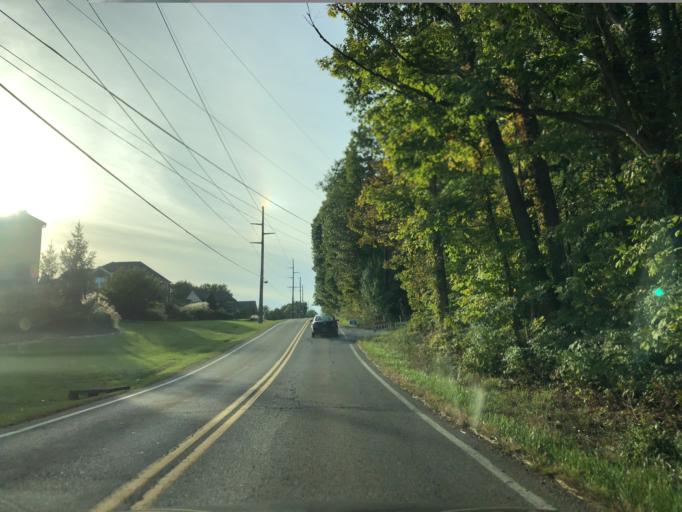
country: US
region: Ohio
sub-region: Warren County
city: Loveland Park
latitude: 39.2890
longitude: -84.2729
